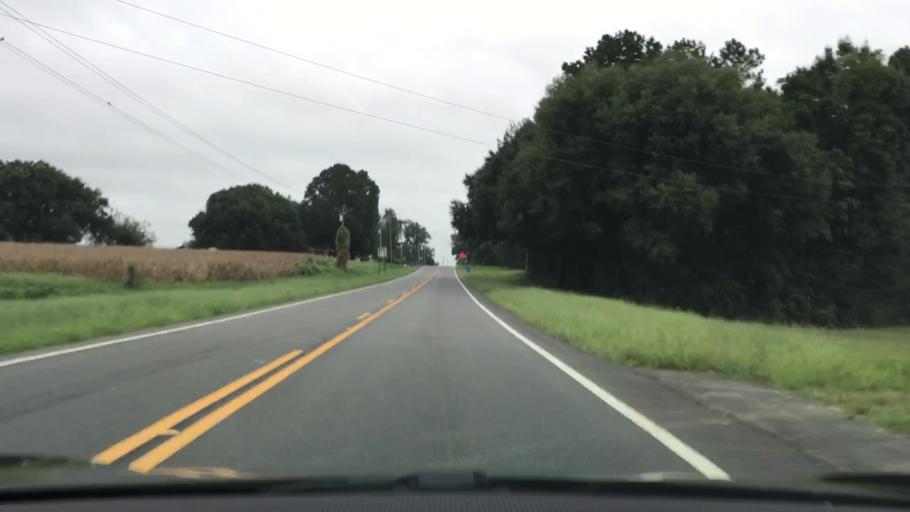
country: US
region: Alabama
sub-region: Covington County
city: Opp
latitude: 31.2763
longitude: -86.1581
